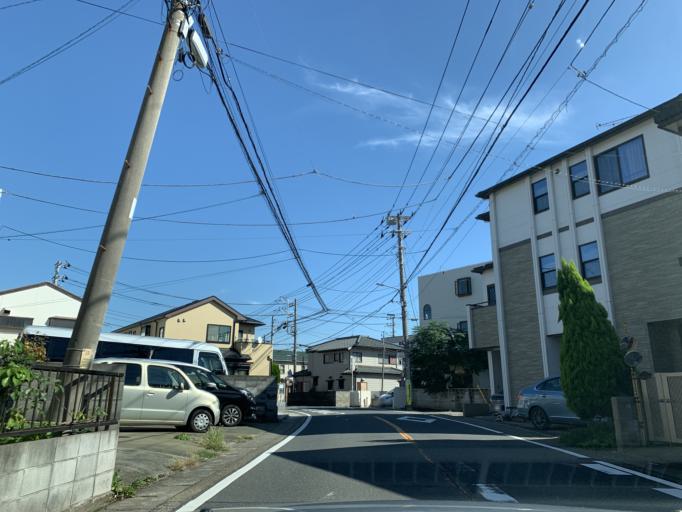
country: JP
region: Tokyo
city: Urayasu
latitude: 35.6814
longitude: 139.9011
